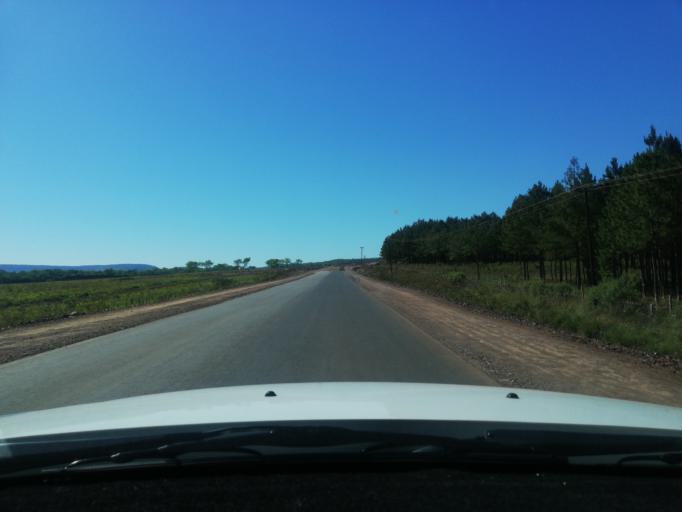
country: AR
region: Misiones
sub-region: Departamento de Candelaria
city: Candelaria
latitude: -27.5277
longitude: -55.7215
